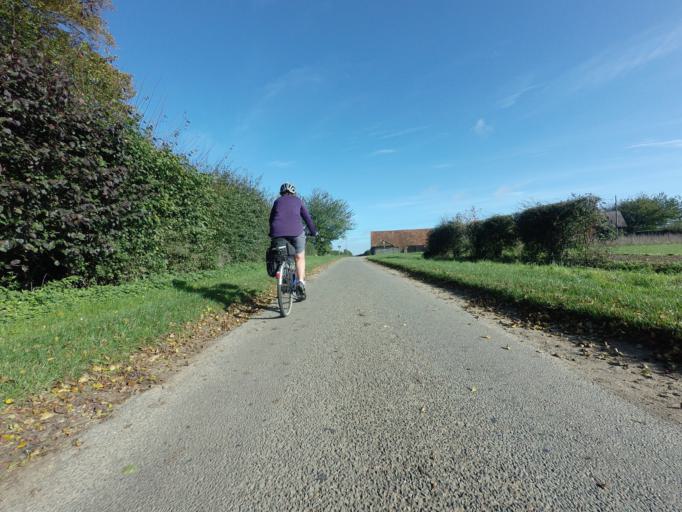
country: GB
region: England
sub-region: Norfolk
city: Dersingham
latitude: 52.8286
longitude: 0.6727
